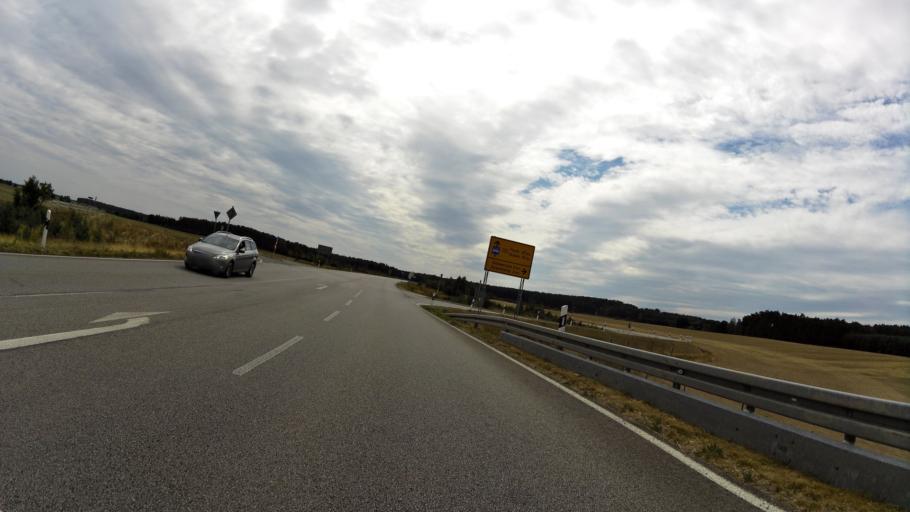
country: DE
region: Brandenburg
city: Neuzelle
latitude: 52.0700
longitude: 14.6613
